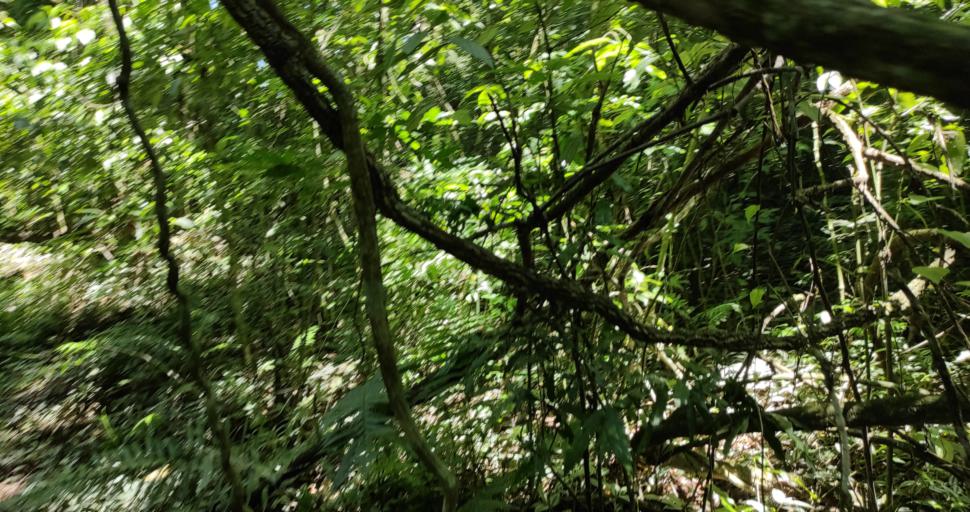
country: BR
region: Rio Grande do Sul
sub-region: Tres Passos
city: Tres Passos
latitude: -27.1524
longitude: -53.9007
